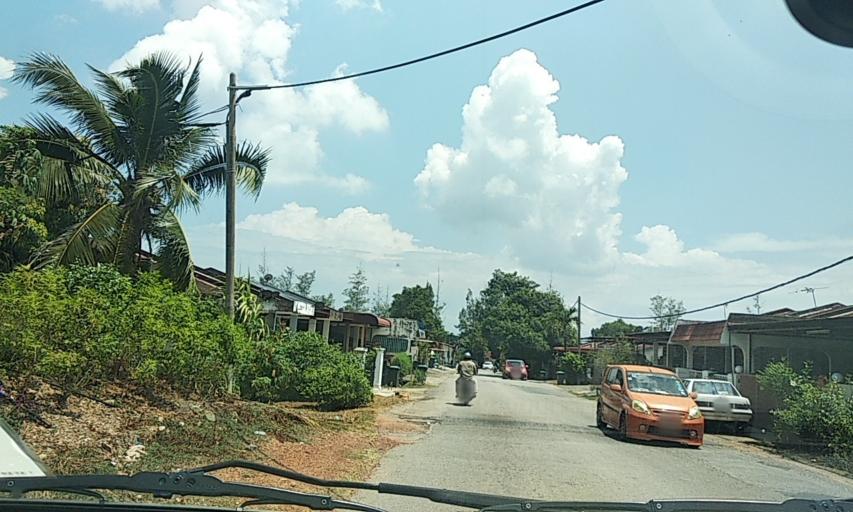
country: MY
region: Kedah
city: Sungai Petani
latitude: 5.6248
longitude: 100.4719
